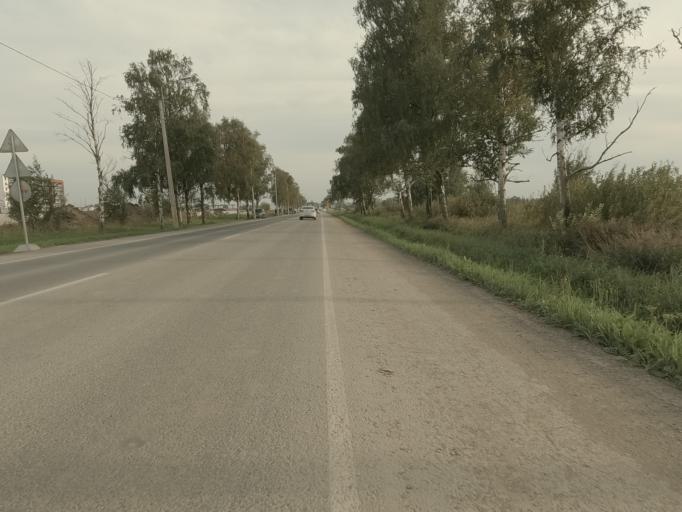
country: RU
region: St.-Petersburg
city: Strel'na
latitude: 59.8445
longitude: 30.0910
